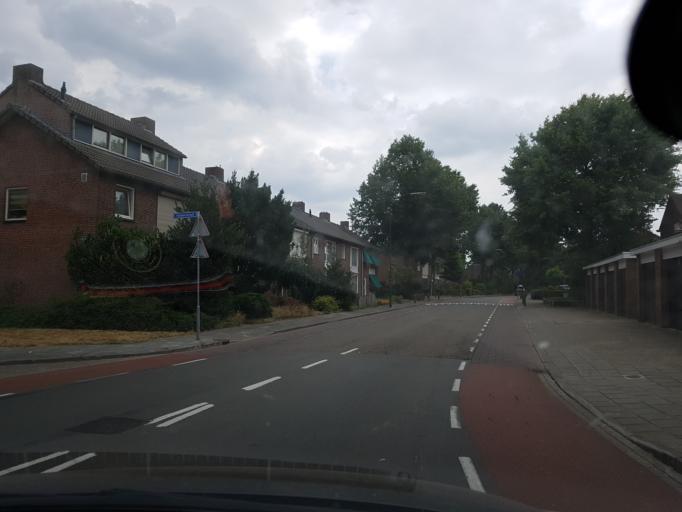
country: NL
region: North Brabant
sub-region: Gemeente Geldrop-Mierlo
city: Geldrop
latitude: 51.4309
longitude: 5.5652
